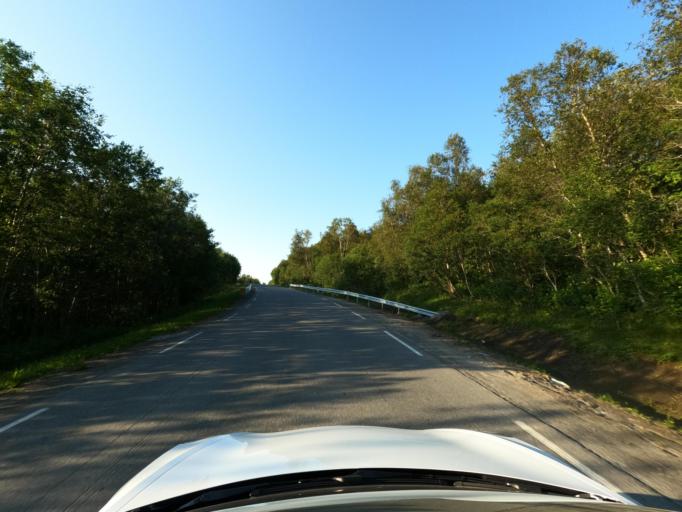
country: NO
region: Troms
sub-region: Skanland
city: Evenskjer
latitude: 68.4880
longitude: 16.7143
